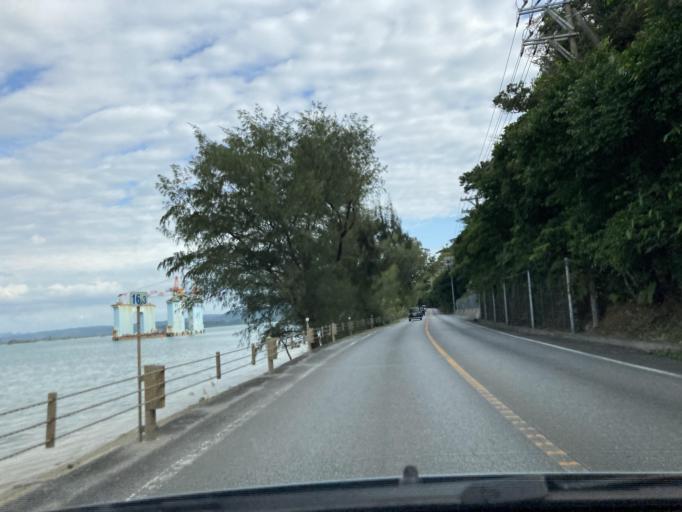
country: JP
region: Okinawa
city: Nago
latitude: 26.6451
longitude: 127.9945
